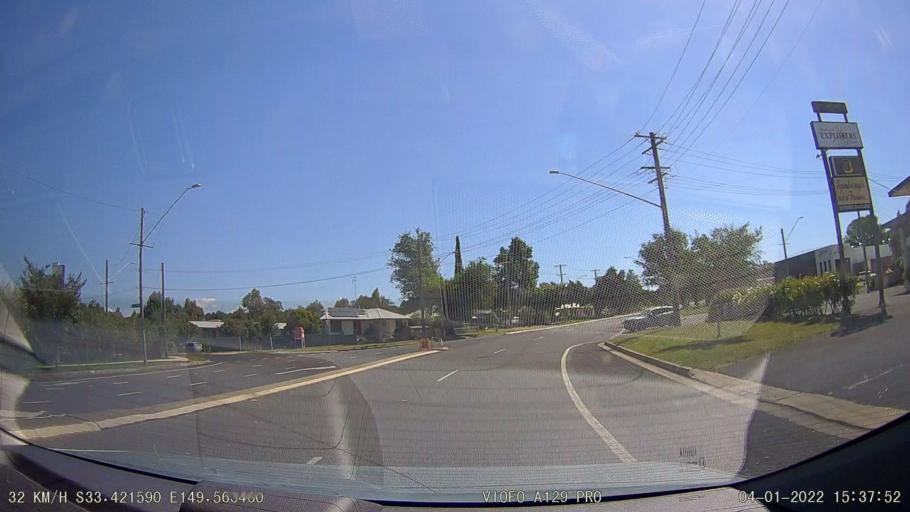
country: AU
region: New South Wales
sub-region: Bathurst Regional
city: Bathurst
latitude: -33.4215
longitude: 149.5637
